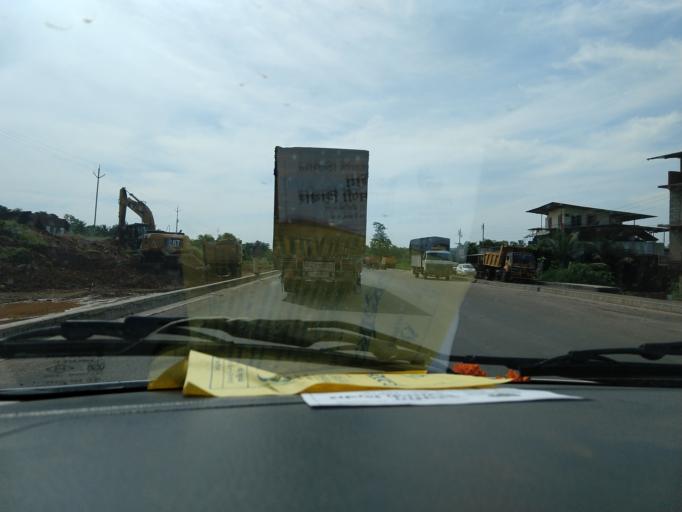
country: IN
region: Maharashtra
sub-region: Sindhudurg
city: Kudal
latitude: 15.9918
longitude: 73.6988
